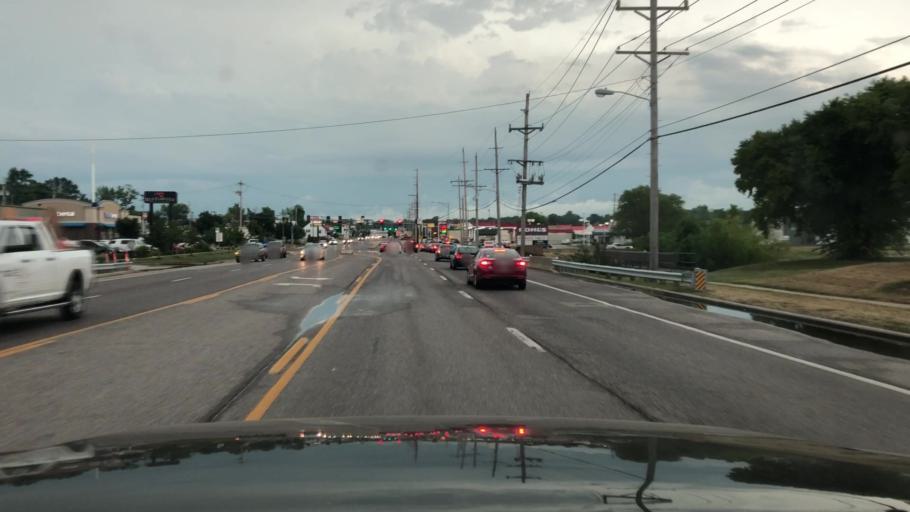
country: US
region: Missouri
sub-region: Saint Louis County
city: Bridgeton
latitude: 38.7524
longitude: -90.4277
